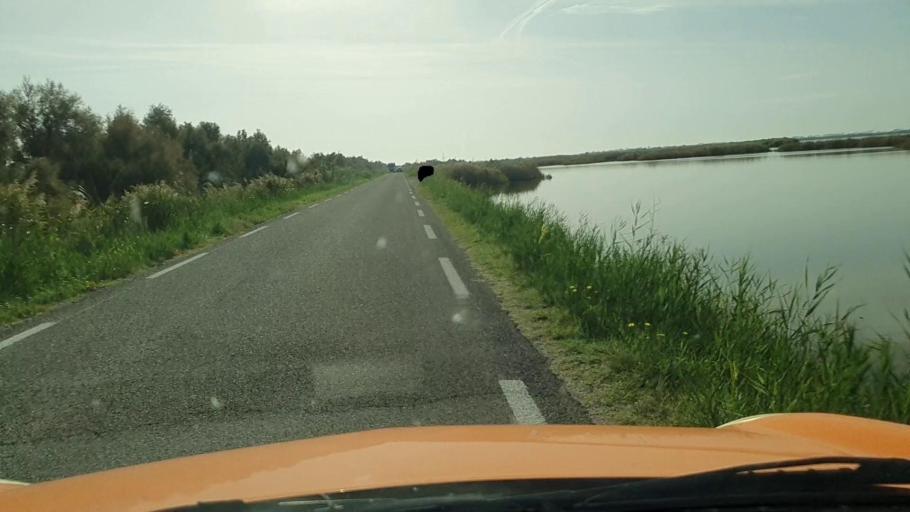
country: FR
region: Languedoc-Roussillon
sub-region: Departement du Gard
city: Vauvert
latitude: 43.6266
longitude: 4.3109
